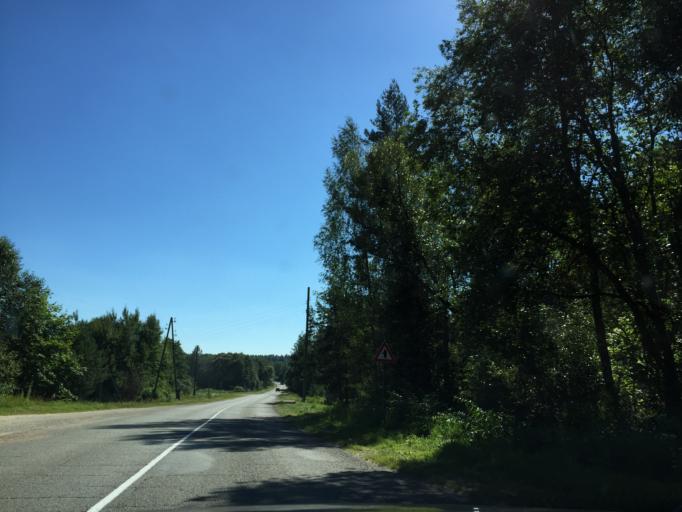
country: LV
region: Akniste
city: Akniste
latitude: 56.1267
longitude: 25.8311
